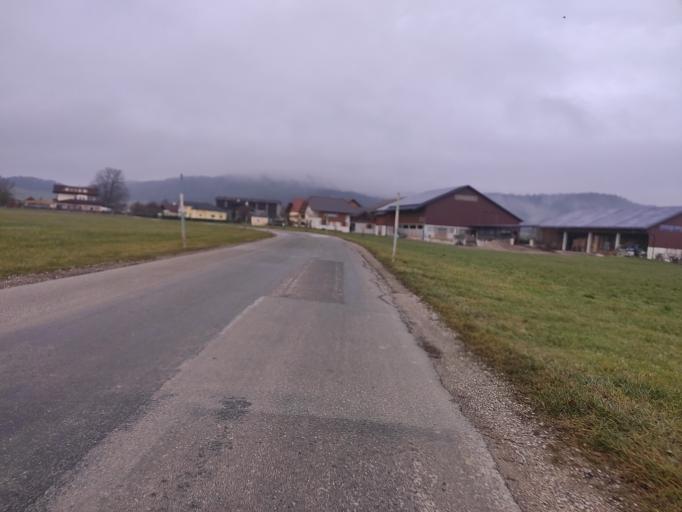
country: AT
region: Salzburg
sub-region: Politischer Bezirk Salzburg-Umgebung
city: Neumarkt am Wallersee
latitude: 47.9694
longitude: 13.2221
